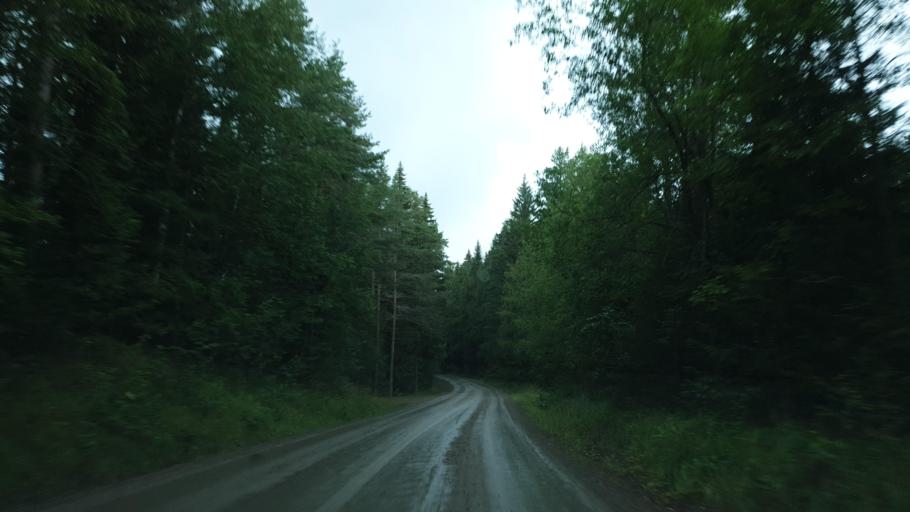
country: FI
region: Northern Savo
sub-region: Kuopio
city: Nilsiae
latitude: 63.1525
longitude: 28.1998
